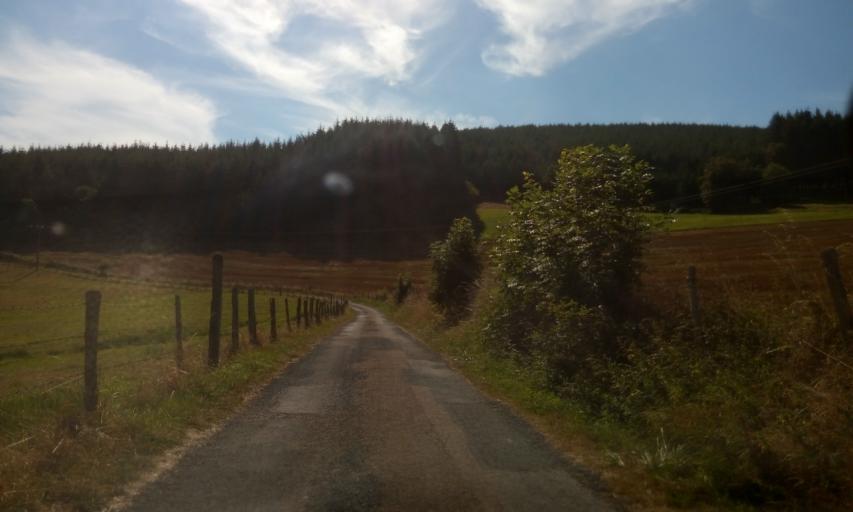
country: FR
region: Rhone-Alpes
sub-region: Departement du Rhone
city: Amplepuis
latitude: 45.9655
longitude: 4.3518
